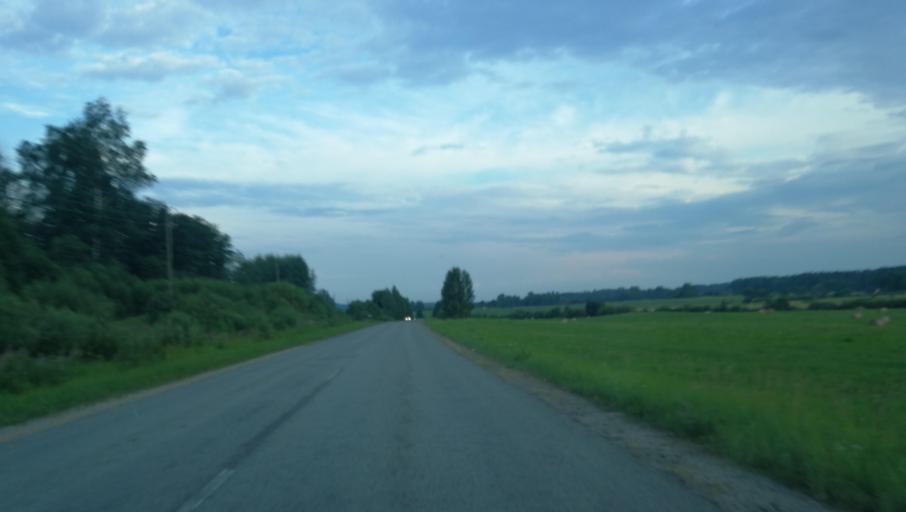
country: LV
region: Cesu Rajons
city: Cesis
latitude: 57.2879
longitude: 25.3107
